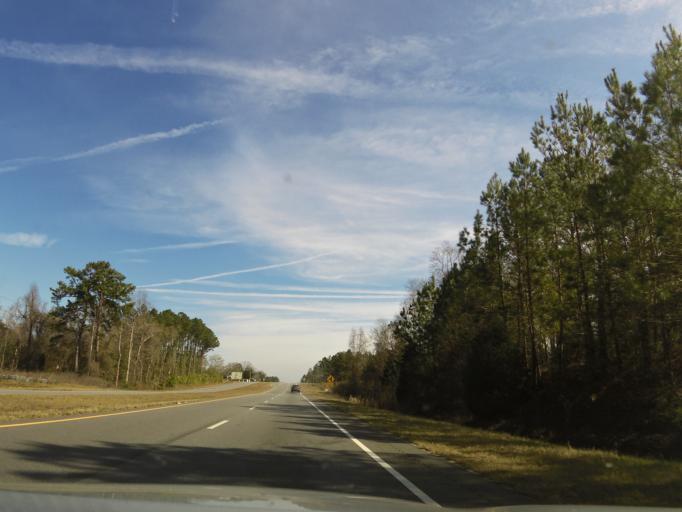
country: US
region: Georgia
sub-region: Brantley County
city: Nahunta
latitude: 31.2155
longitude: -81.8949
